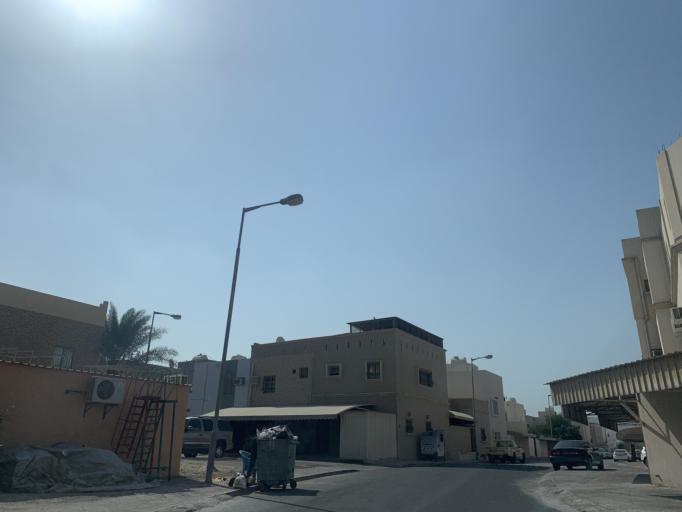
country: BH
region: Central Governorate
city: Madinat Hamad
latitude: 26.1307
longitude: 50.5043
